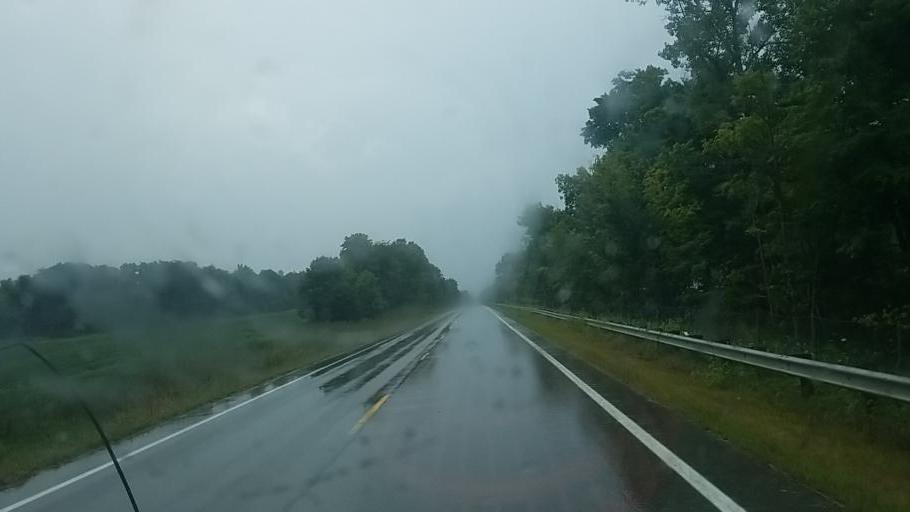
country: US
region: Ohio
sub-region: Champaign County
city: North Lewisburg
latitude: 40.3264
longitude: -83.6127
